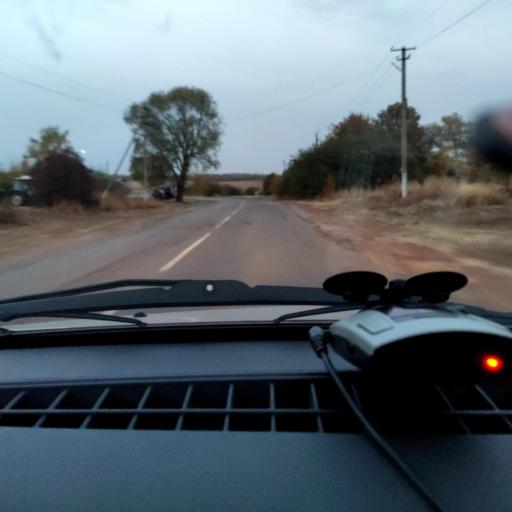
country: RU
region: Voronezj
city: Kolodeznyy
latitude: 51.2386
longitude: 39.0401
